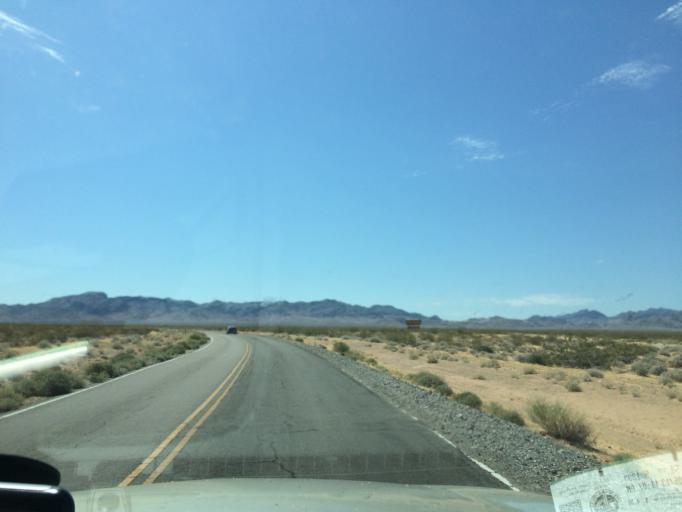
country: US
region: Nevada
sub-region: Clark County
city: Moapa Town
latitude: 36.4607
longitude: -114.7357
